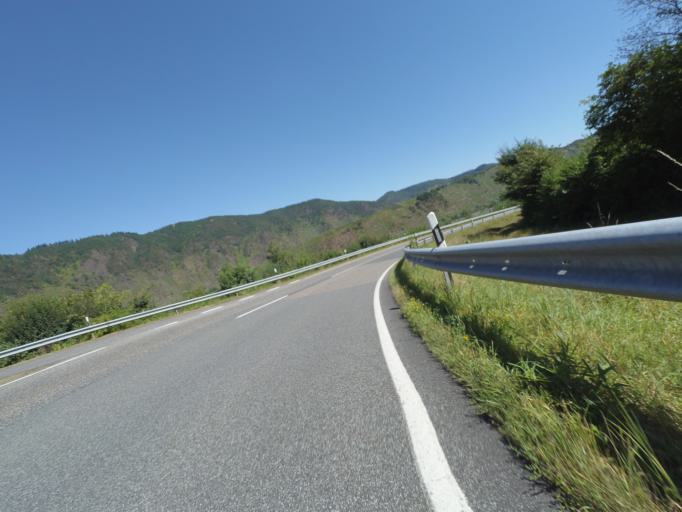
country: DE
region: Rheinland-Pfalz
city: Bremm
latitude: 50.0974
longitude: 7.1166
